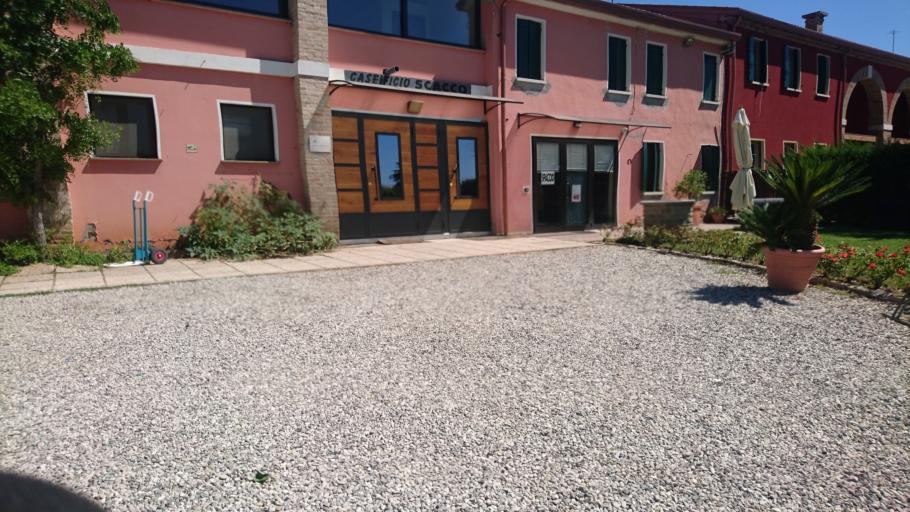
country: IT
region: Veneto
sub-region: Provincia di Padova
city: Pontelongo
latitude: 45.2574
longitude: 12.0171
